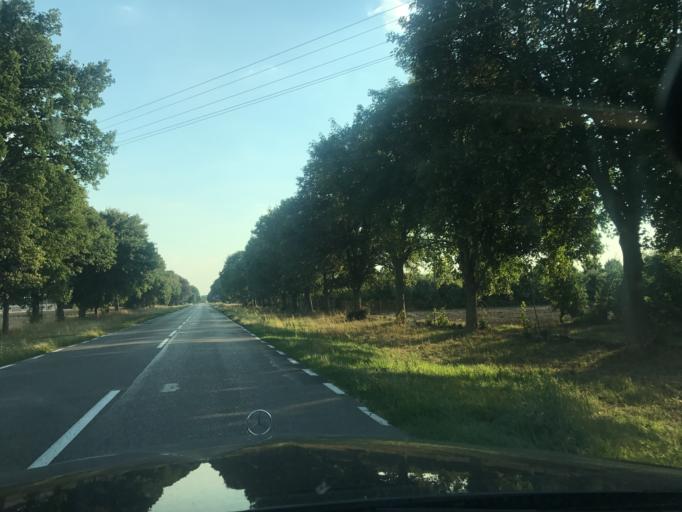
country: PL
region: Lublin Voivodeship
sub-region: Powiat bialski
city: Wisznice
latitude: 51.7598
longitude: 23.1806
